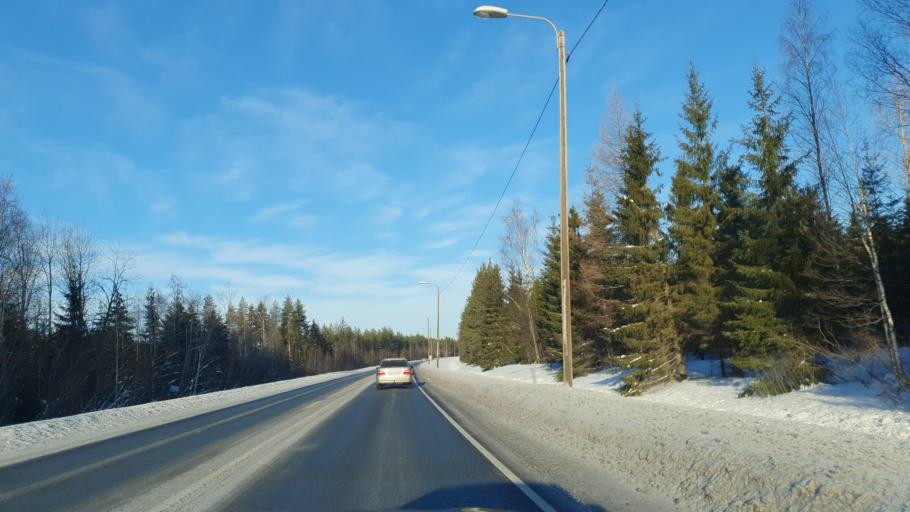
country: FI
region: Northern Ostrobothnia
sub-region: Oulu
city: Kempele
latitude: 64.9591
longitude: 25.6448
